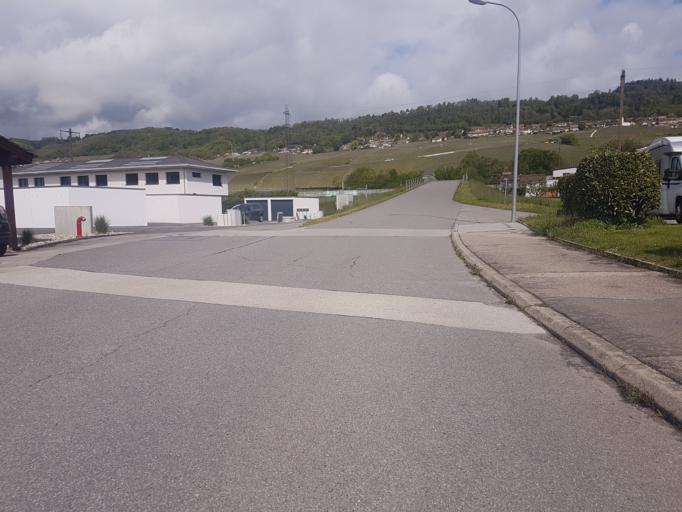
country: CH
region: Vaud
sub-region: Nyon District
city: Perroy
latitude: 46.4698
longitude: 6.3597
